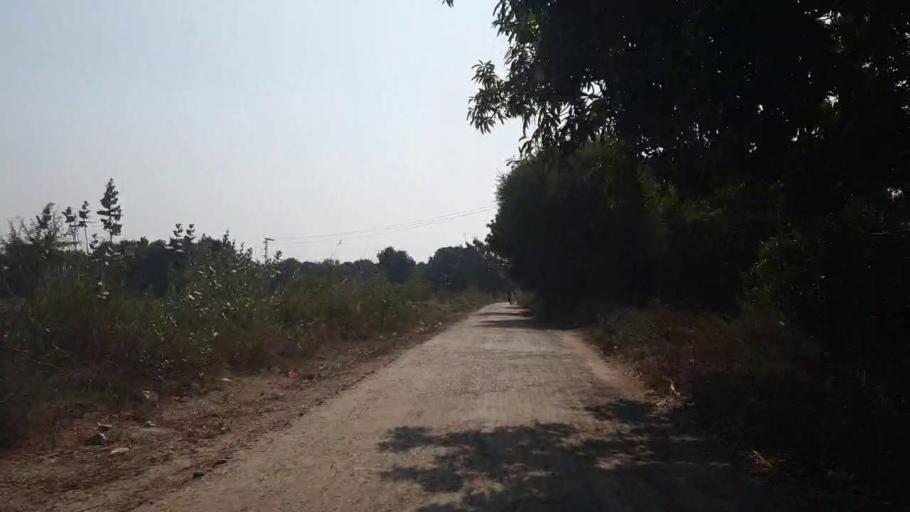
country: PK
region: Sindh
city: Tando Allahyar
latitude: 25.4870
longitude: 68.8481
